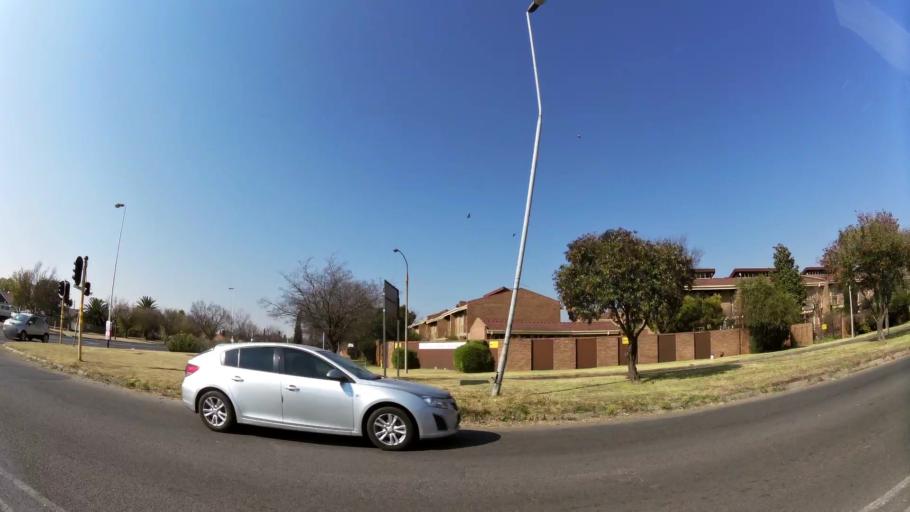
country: ZA
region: Gauteng
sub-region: Ekurhuleni Metropolitan Municipality
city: Boksburg
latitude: -26.2415
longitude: 28.2641
